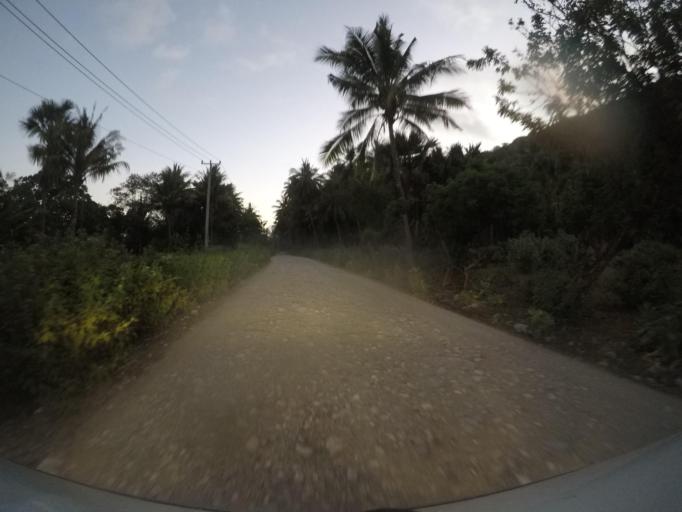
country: TL
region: Viqueque
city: Viqueque
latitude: -8.7960
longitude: 126.6232
